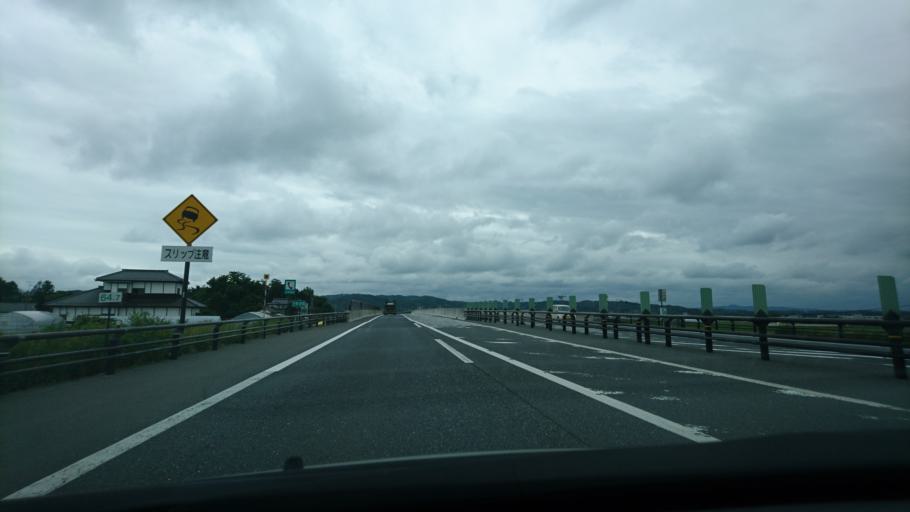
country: JP
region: Miyagi
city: Wakuya
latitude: 38.6686
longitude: 141.2658
